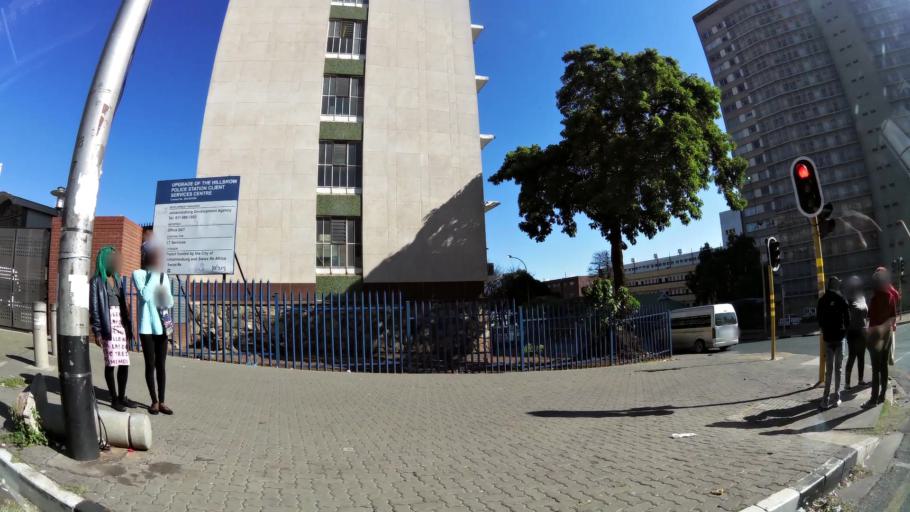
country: ZA
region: Gauteng
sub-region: City of Johannesburg Metropolitan Municipality
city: Johannesburg
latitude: -26.1873
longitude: 28.0455
